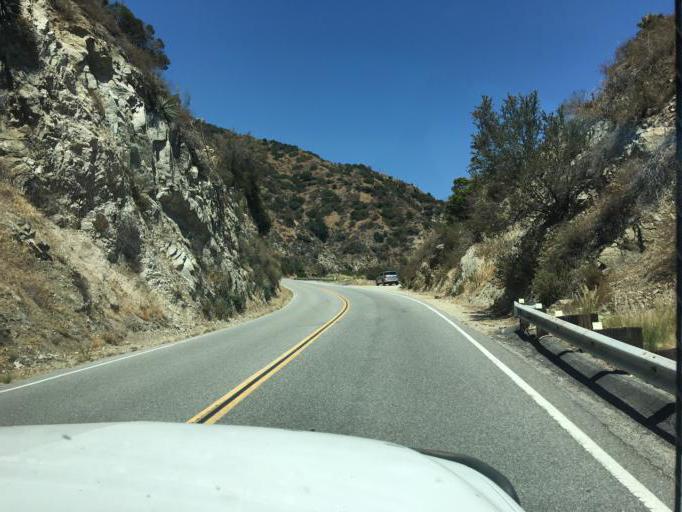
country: US
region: California
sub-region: Los Angeles County
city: Glendora
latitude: 34.1726
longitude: -117.8872
